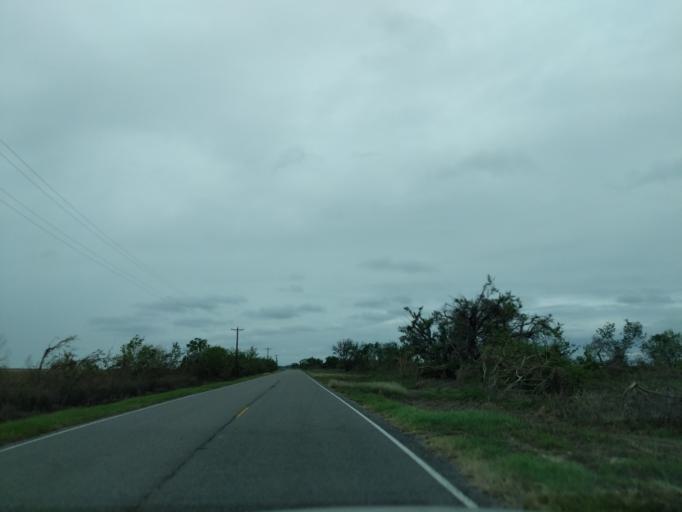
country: US
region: Louisiana
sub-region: Cameron Parish
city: Cameron
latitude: 29.7868
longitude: -93.1512
